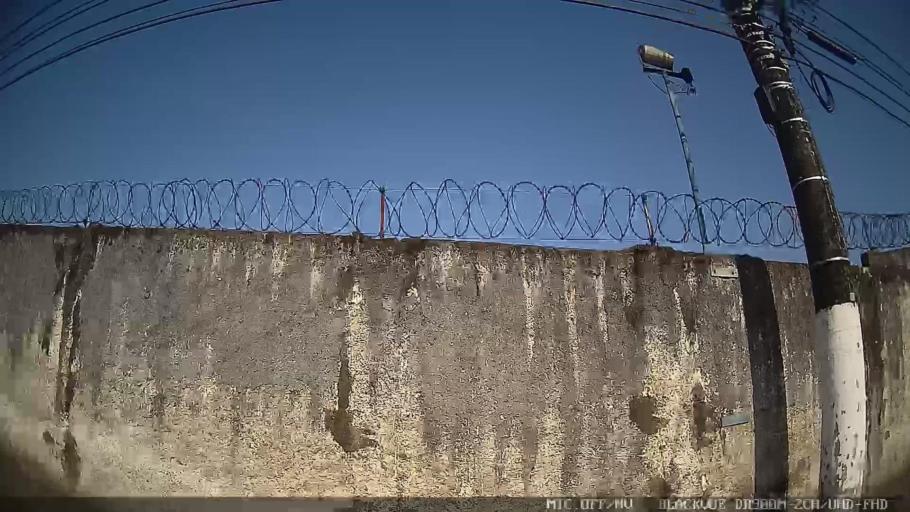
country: BR
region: Sao Paulo
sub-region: Guaruja
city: Guaruja
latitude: -23.9853
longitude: -46.2731
